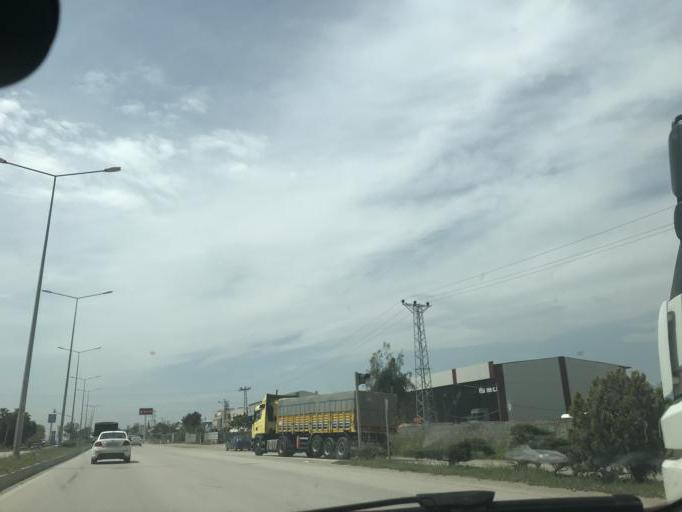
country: TR
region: Adana
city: Yuregir
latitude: 36.9815
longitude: 35.4401
